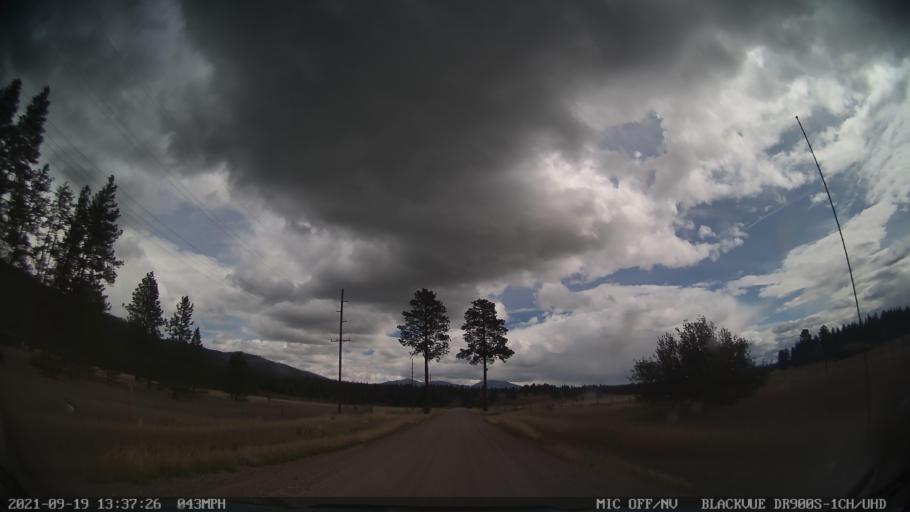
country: US
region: Montana
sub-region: Missoula County
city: Seeley Lake
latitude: 47.1066
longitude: -113.2833
